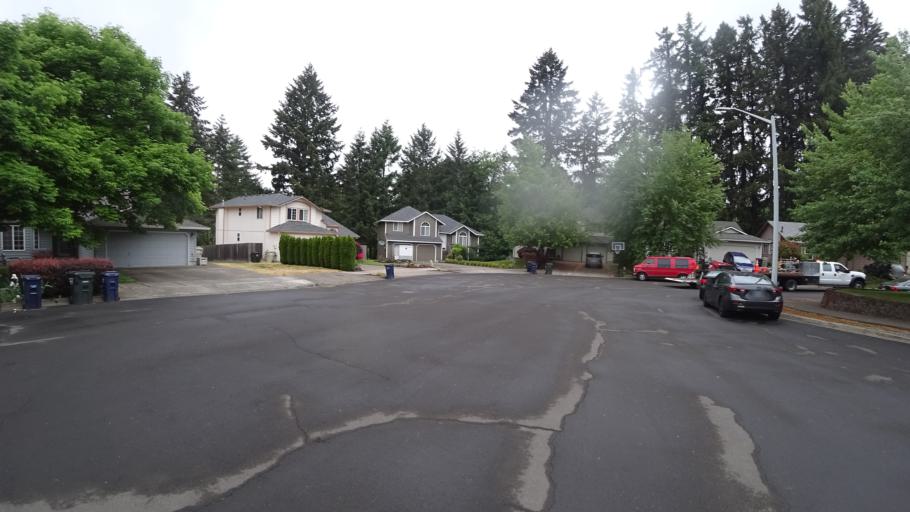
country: US
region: Oregon
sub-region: Washington County
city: Rockcreek
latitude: 45.5317
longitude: -122.8929
